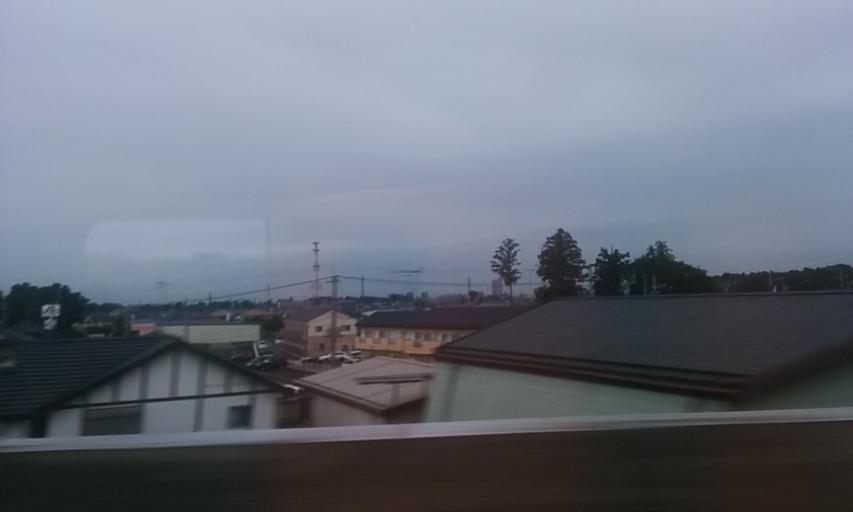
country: JP
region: Ibaraki
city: Koga
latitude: 36.1820
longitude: 139.7403
